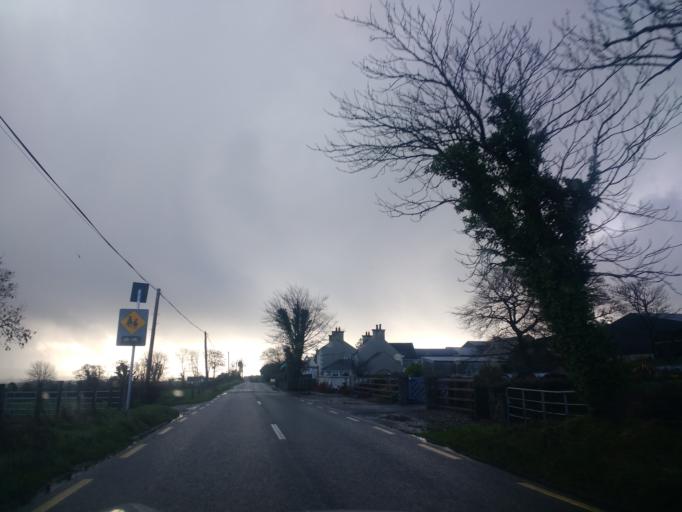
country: IE
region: Ulster
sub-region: County Donegal
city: Ramelton
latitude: 55.0109
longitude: -7.6568
